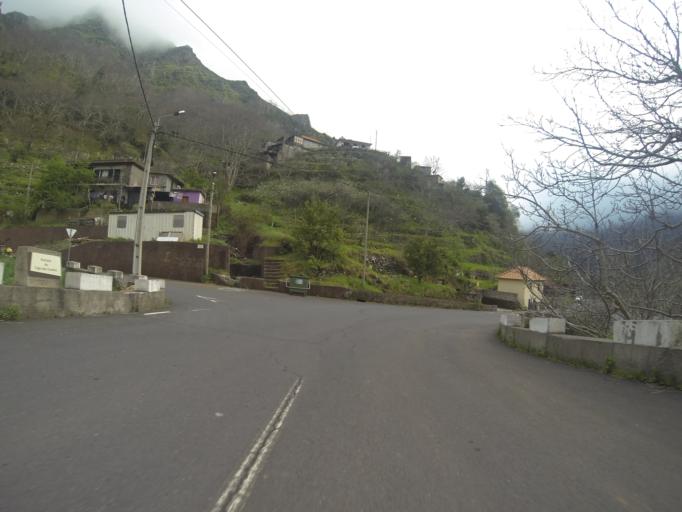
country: PT
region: Madeira
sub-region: Camara de Lobos
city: Curral das Freiras
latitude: 32.7406
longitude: -16.9682
